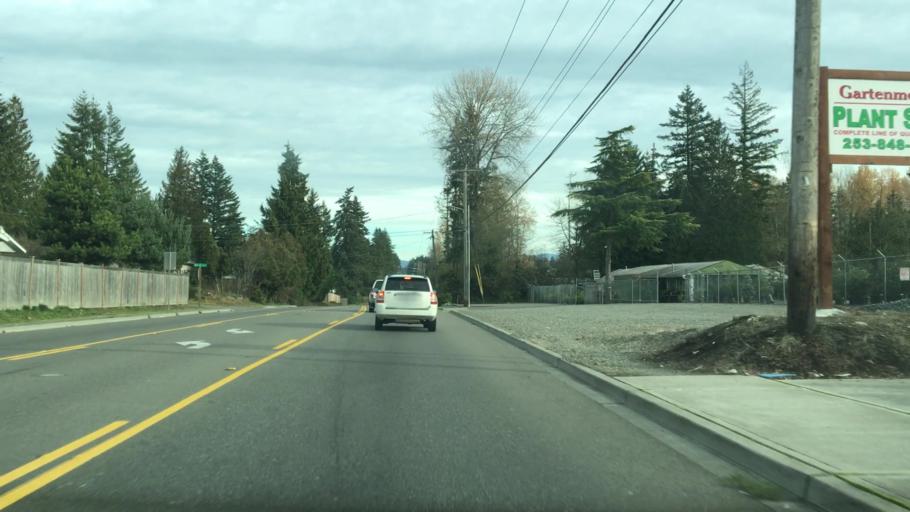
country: US
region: Washington
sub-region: Pierce County
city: Frederickson
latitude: 47.1111
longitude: -122.3216
